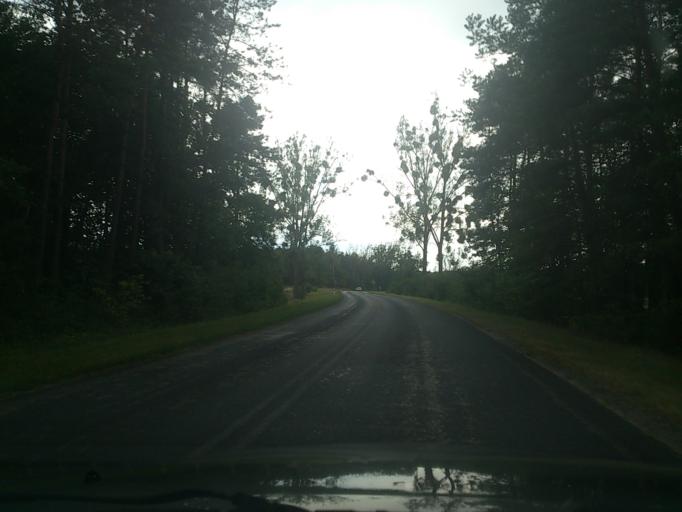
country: PL
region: Kujawsko-Pomorskie
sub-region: Powiat golubsko-dobrzynski
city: Golub-Dobrzyn
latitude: 53.0879
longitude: 19.0534
